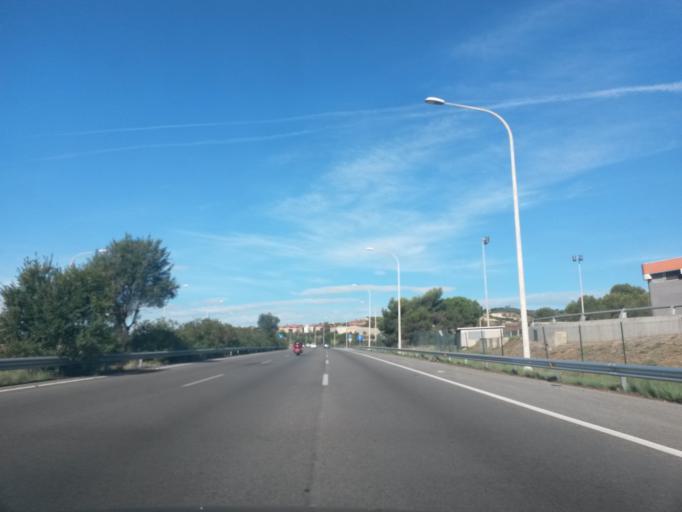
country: ES
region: Catalonia
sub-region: Provincia de Barcelona
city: Teia
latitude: 41.4926
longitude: 2.3345
